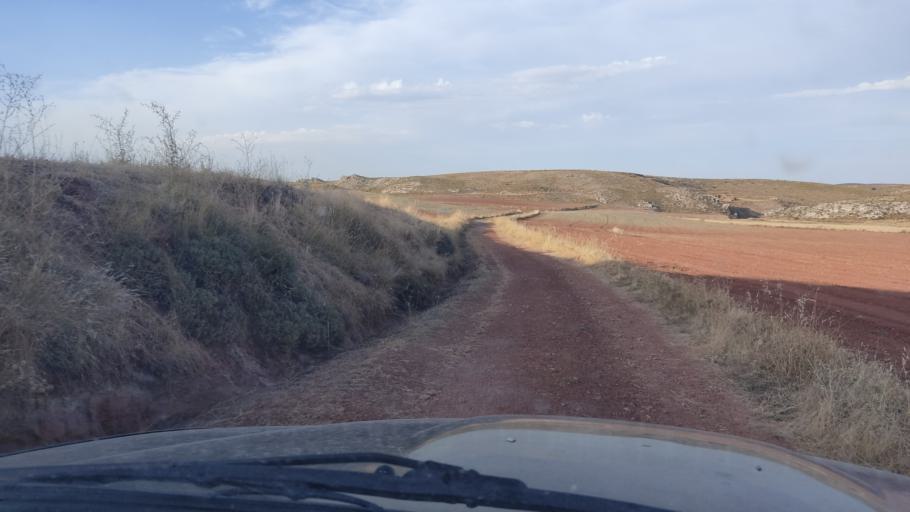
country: ES
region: Aragon
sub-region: Provincia de Teruel
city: Monforte de Moyuela
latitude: 41.0488
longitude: -0.9692
